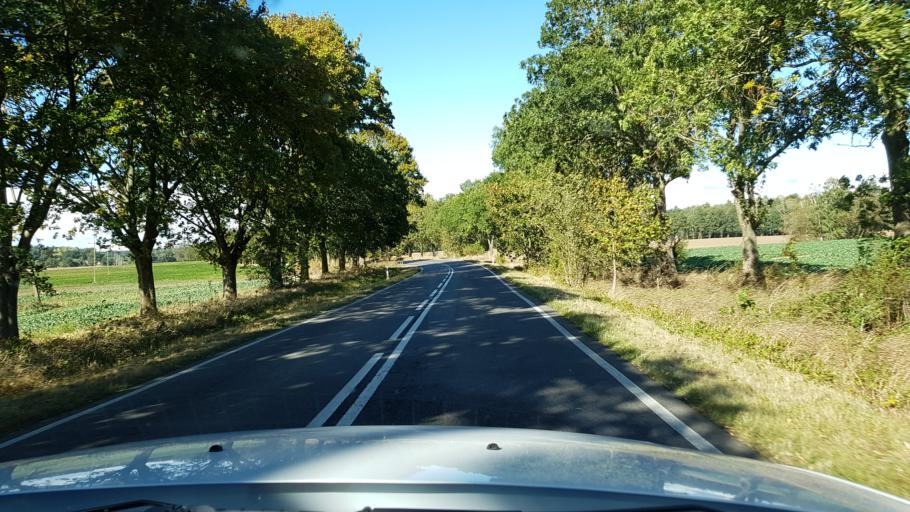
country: PL
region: West Pomeranian Voivodeship
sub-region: Powiat gryfinski
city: Banie
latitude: 53.1535
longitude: 14.6052
